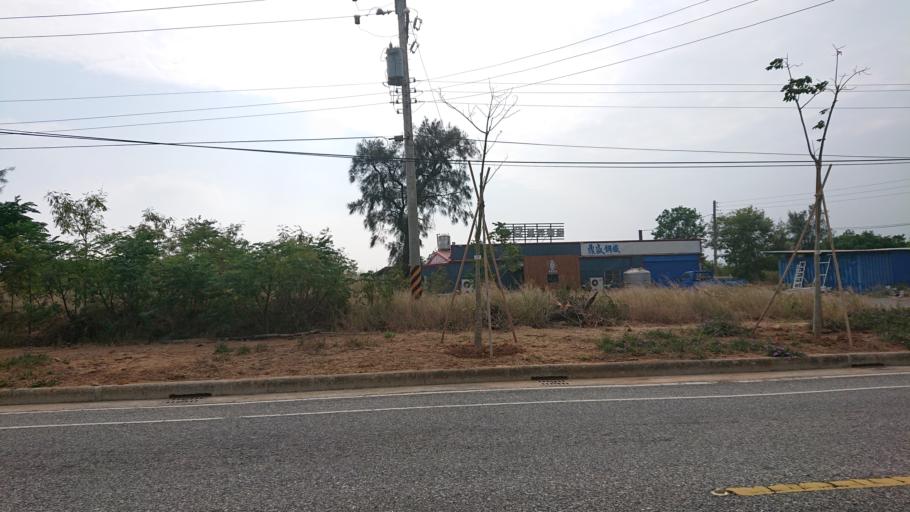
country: TW
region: Fukien
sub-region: Kinmen
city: Jincheng
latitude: 24.4540
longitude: 118.3792
